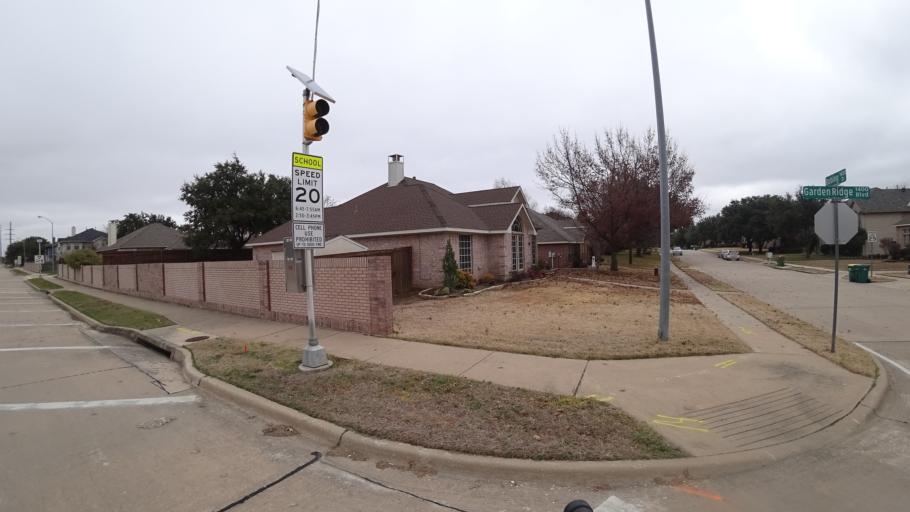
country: US
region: Texas
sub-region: Denton County
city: Lewisville
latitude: 33.0289
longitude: -97.0361
